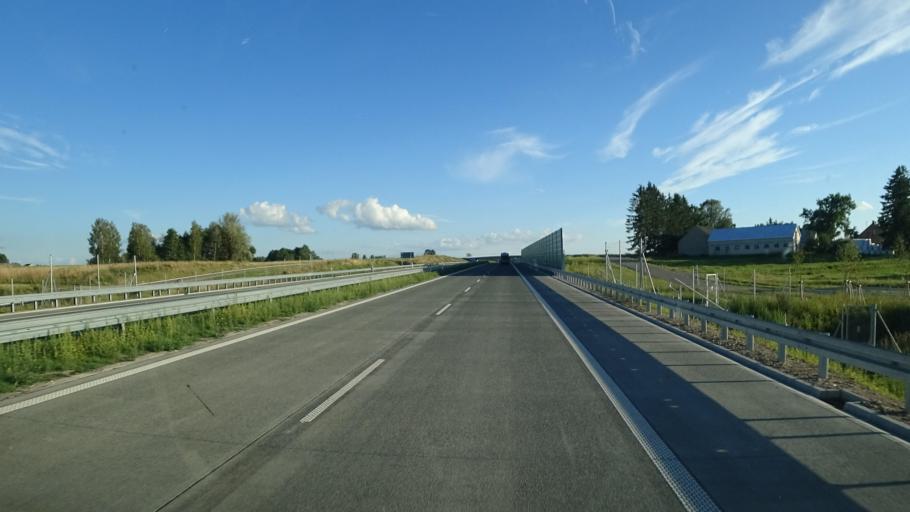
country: PL
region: Podlasie
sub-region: Powiat suwalski
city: Raczki
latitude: 53.9470
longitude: 22.7655
